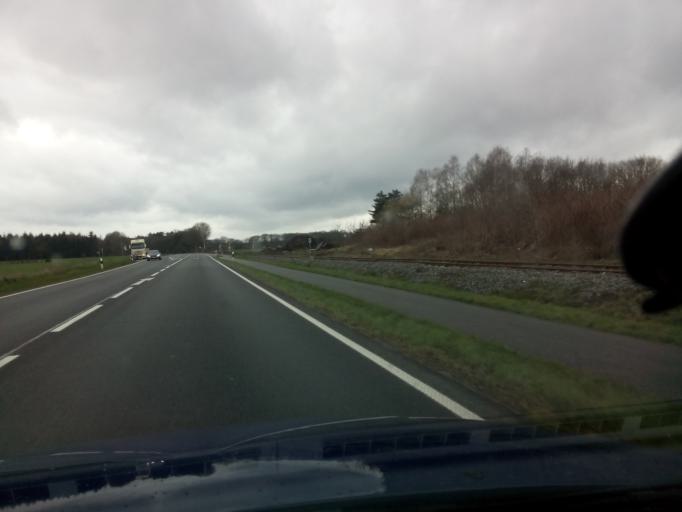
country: DE
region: Lower Saxony
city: Herzlake
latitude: 52.6946
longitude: 7.5596
